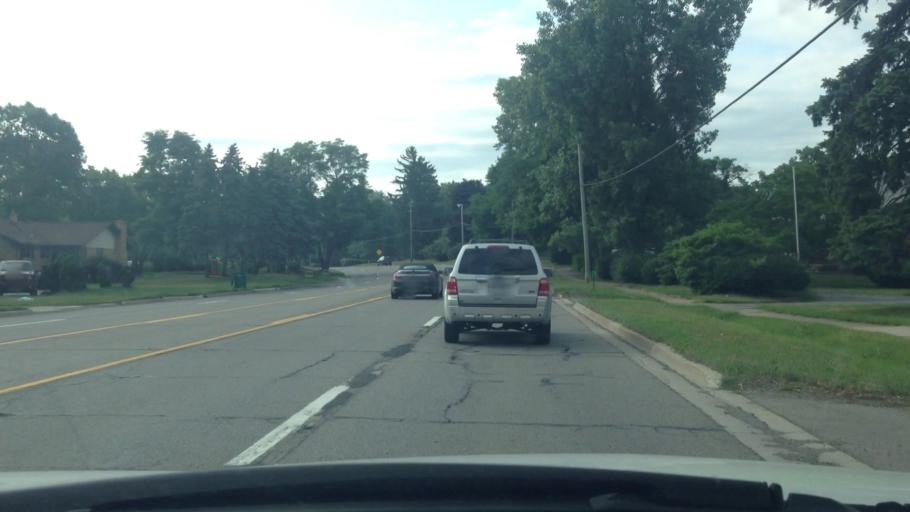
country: US
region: Michigan
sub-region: Oakland County
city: Waterford
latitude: 42.6852
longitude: -83.3442
